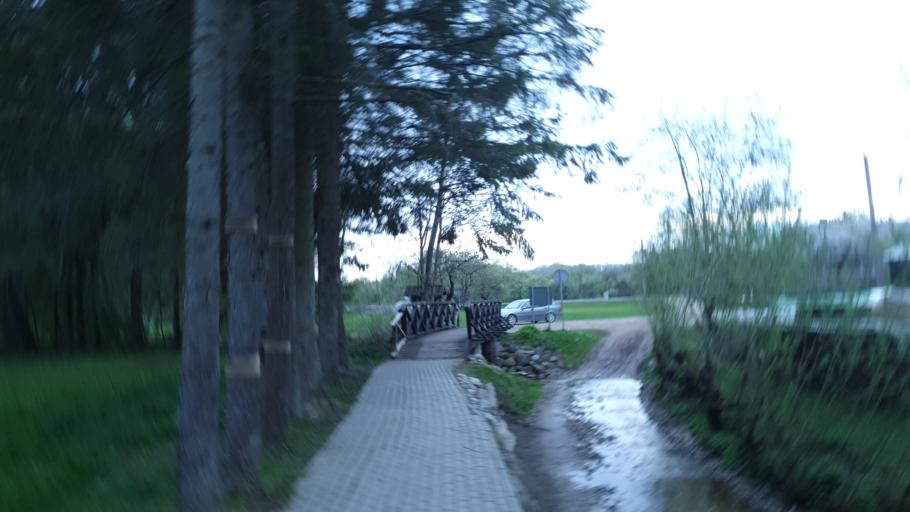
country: LT
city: Sakiai
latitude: 55.0823
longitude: 23.1779
